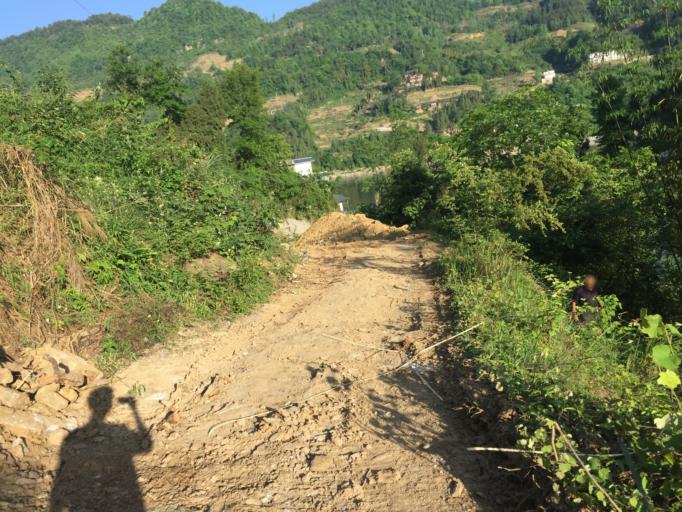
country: CN
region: Guizhou Sheng
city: Xujiaba
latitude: 27.7119
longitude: 108.0262
